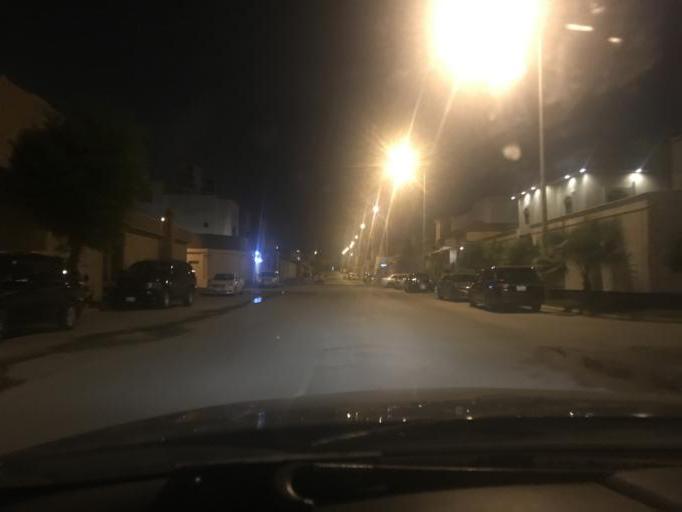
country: SA
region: Ar Riyad
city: Riyadh
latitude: 24.7562
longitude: 46.7633
